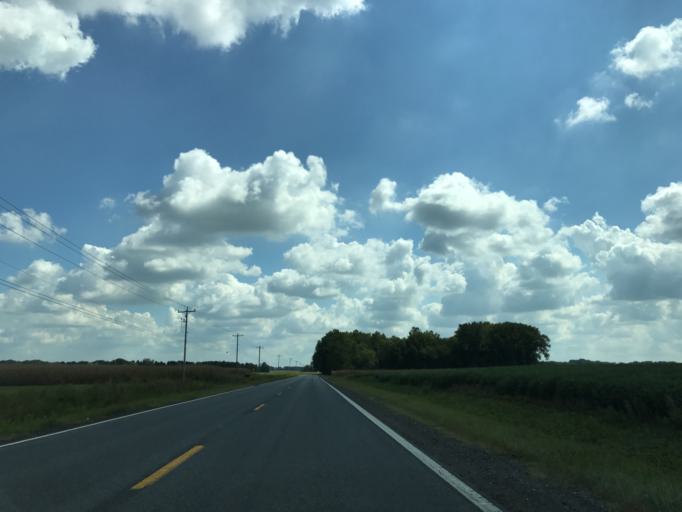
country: US
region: Maryland
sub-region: Queen Anne's County
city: Centreville
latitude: 39.0084
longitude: -75.9874
